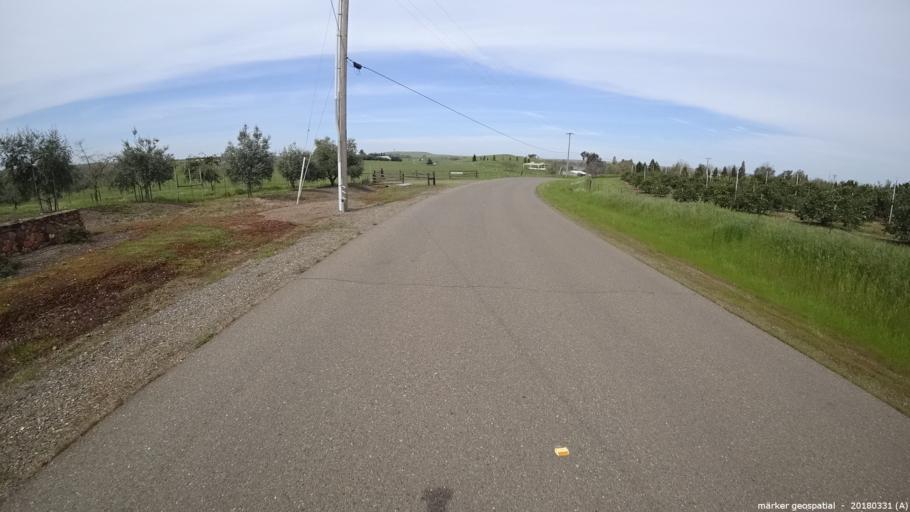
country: US
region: California
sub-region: Sacramento County
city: Rancho Murieta
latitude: 38.4921
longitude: -121.1472
